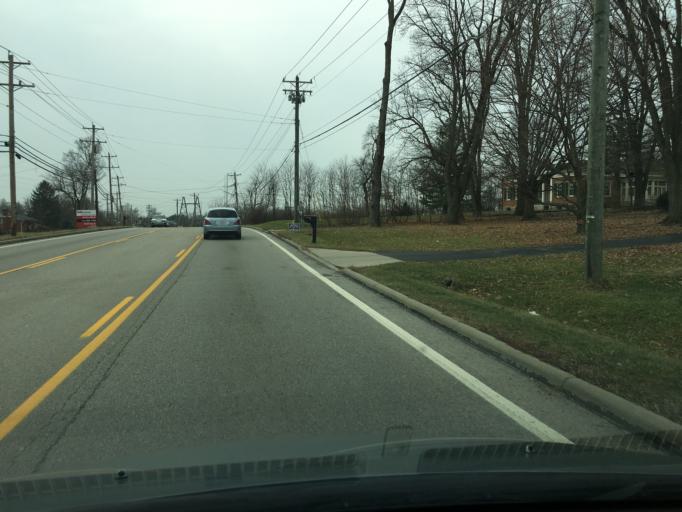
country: US
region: Ohio
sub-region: Hamilton County
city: Highpoint
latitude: 39.3086
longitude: -84.3834
